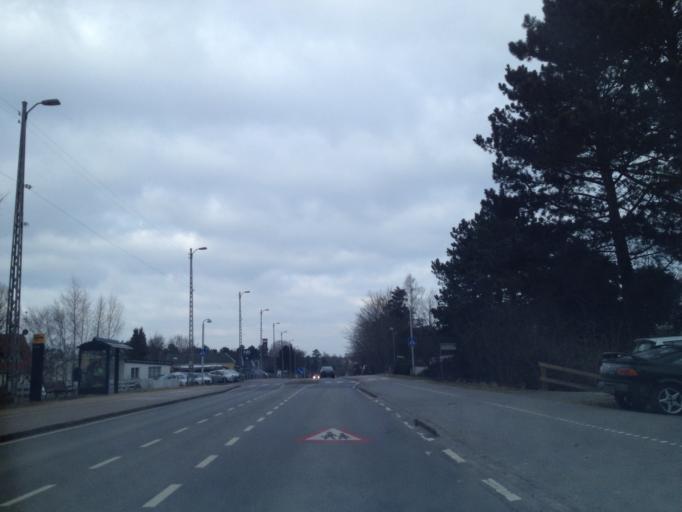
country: DK
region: Capital Region
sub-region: Helsingor Kommune
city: Espergaerde
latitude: 55.9836
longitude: 12.5487
